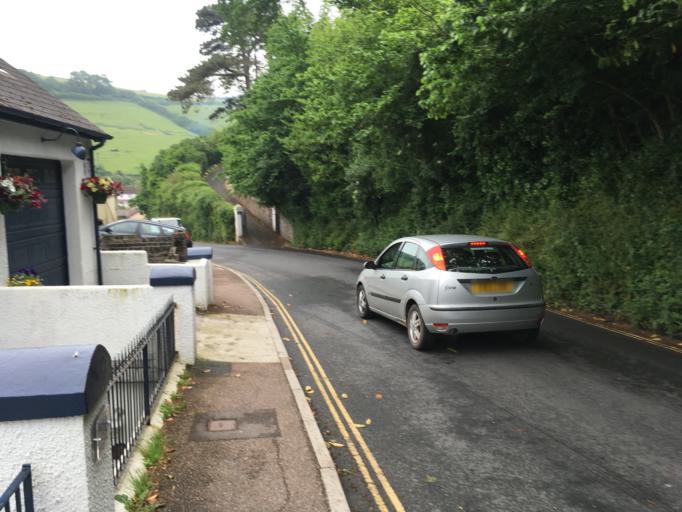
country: GB
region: England
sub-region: Devon
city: Dartmouth
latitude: 50.3506
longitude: -3.5890
